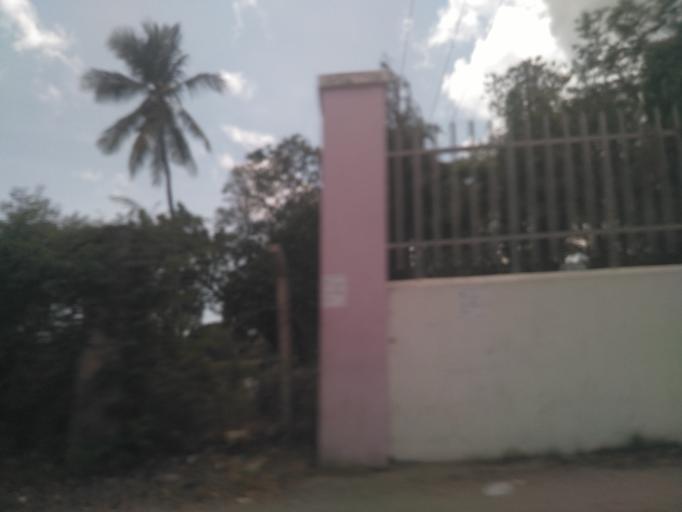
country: TZ
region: Dar es Salaam
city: Dar es Salaam
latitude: -6.8519
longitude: 39.2716
